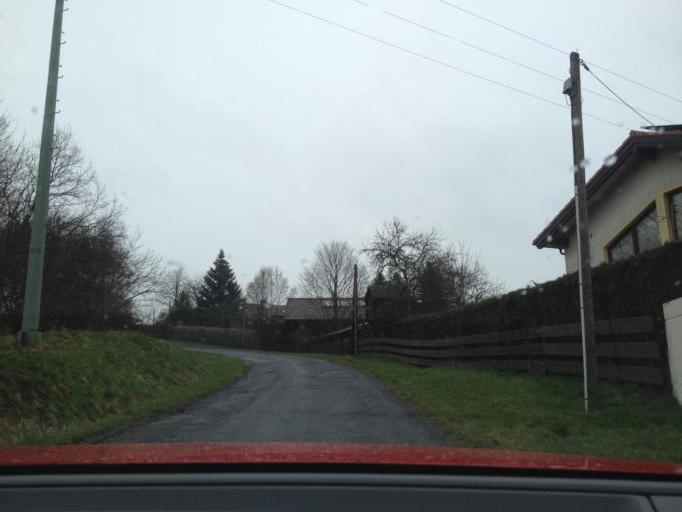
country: DE
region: Bavaria
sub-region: Upper Franconia
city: Thiersheim
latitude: 50.0798
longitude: 12.1425
